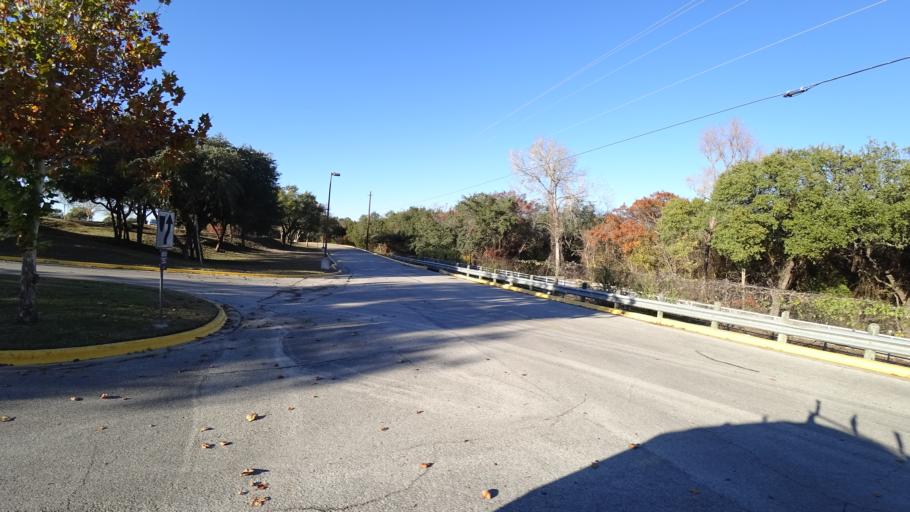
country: US
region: Texas
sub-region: Travis County
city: Wells Branch
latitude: 30.4042
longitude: -97.7034
